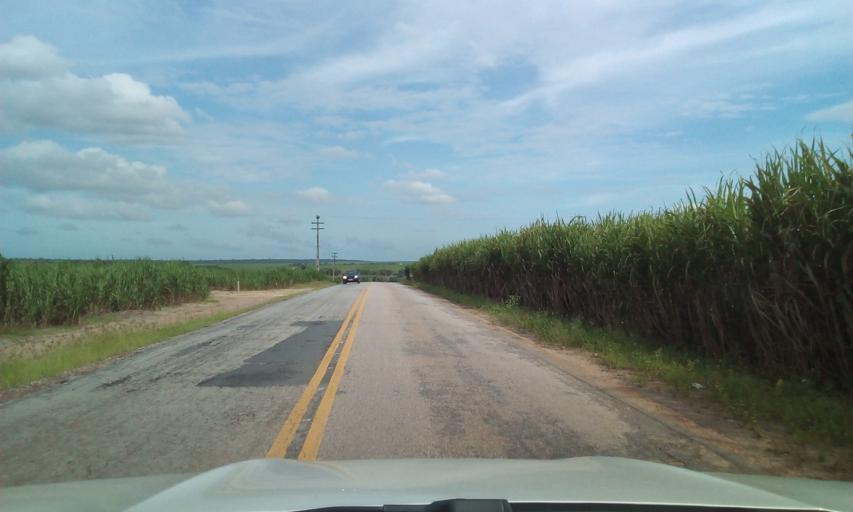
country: BR
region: Paraiba
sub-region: Santa Rita
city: Santa Rita
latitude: -6.9924
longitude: -34.9899
